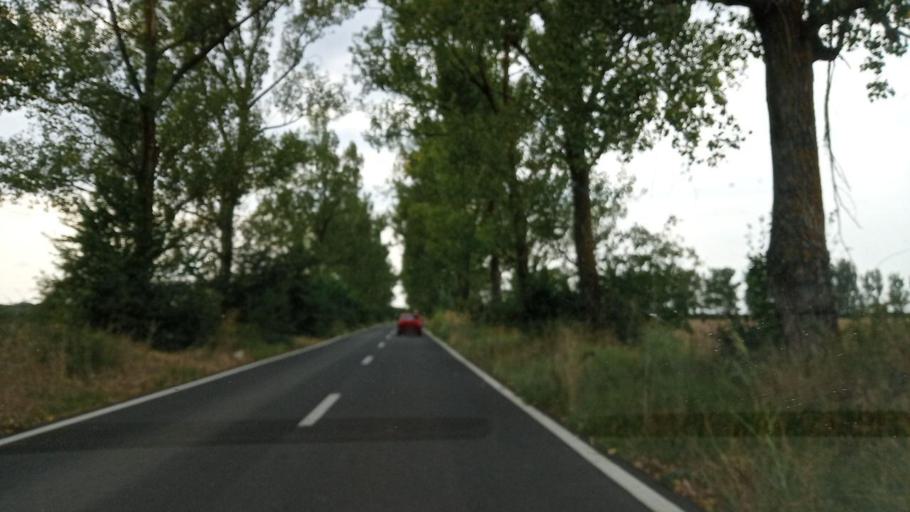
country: RO
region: Giurgiu
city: Gostinari-Vacaresti
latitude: 44.1727
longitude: 26.2136
